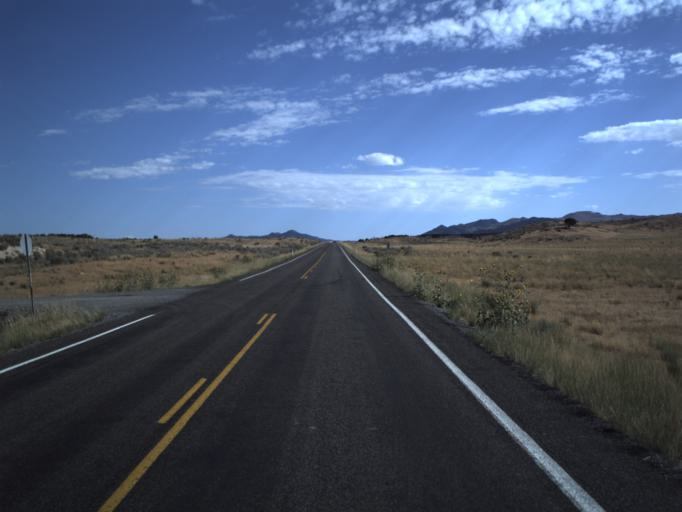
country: US
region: Utah
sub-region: Juab County
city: Mona
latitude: 39.7461
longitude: -112.1859
